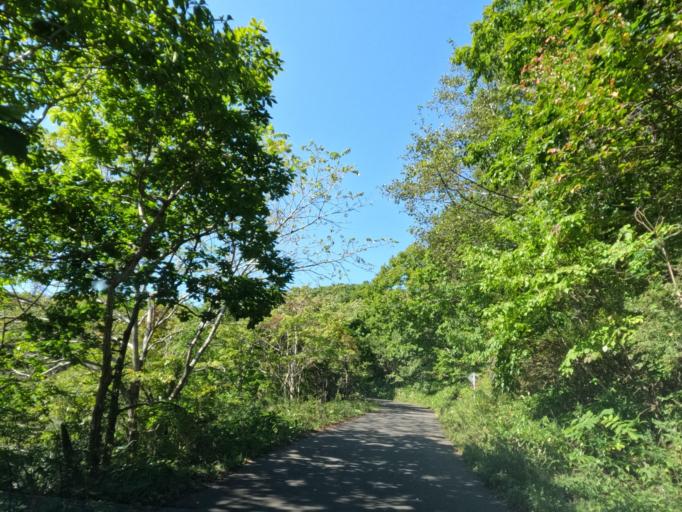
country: JP
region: Hokkaido
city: Muroran
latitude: 42.3660
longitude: 141.0209
